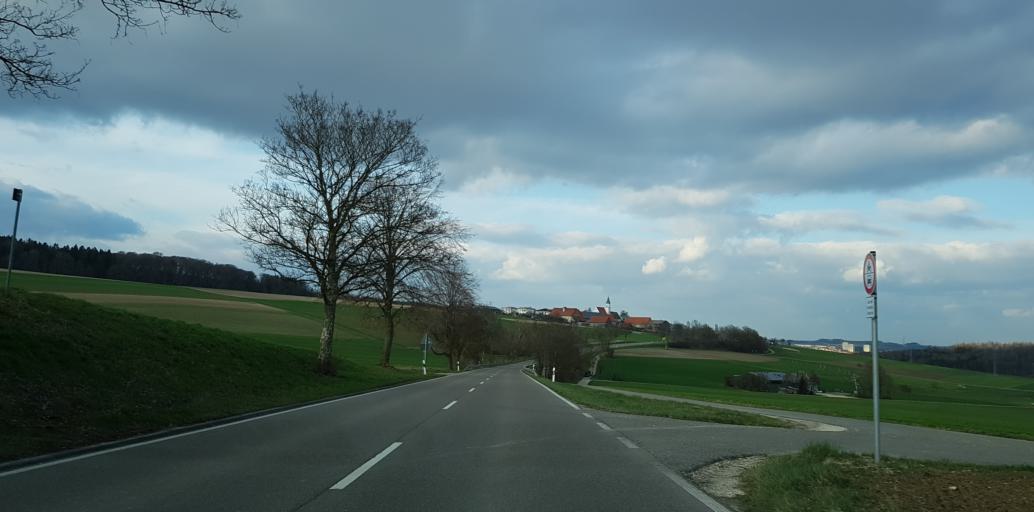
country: DE
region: Baden-Wuerttemberg
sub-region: Tuebingen Region
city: Erbach
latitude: 48.3841
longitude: 9.9064
